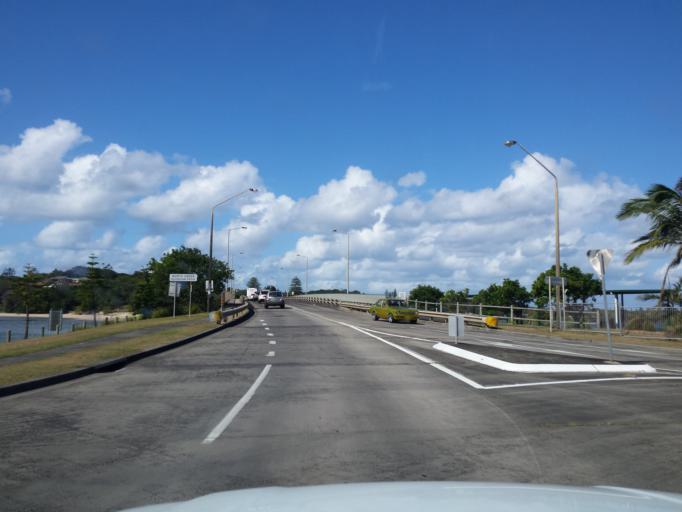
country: AU
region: New South Wales
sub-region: Ballina
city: East Ballina
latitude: -28.8693
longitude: 153.5749
